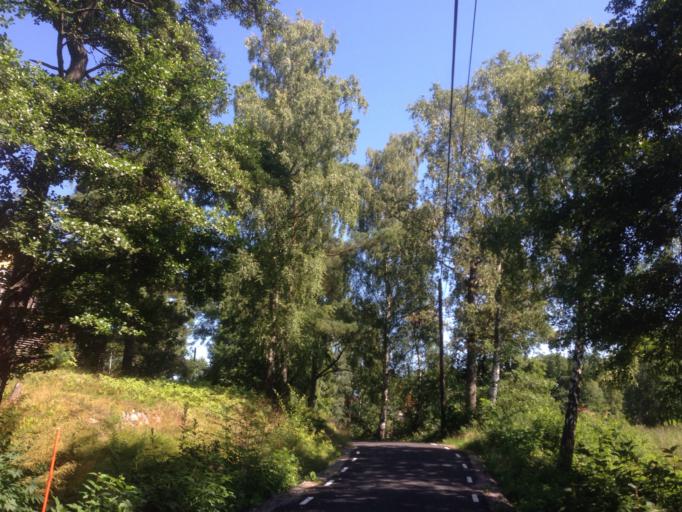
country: SE
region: Stockholm
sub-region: Vaxholms Kommun
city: Vaxholm
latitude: 59.3880
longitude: 18.3726
